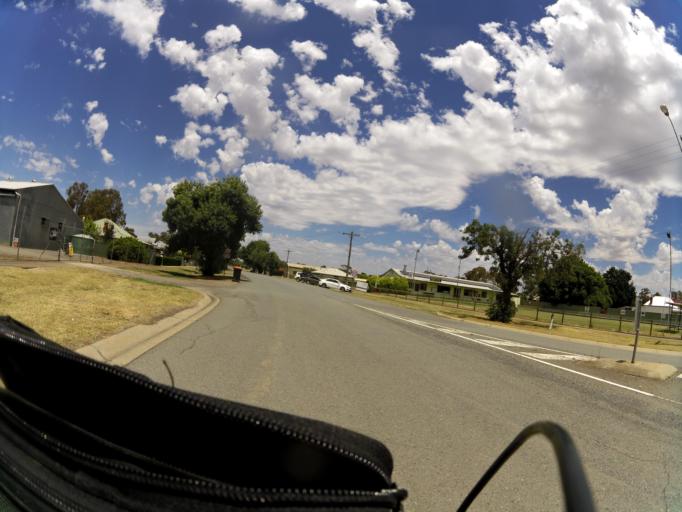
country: AU
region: Victoria
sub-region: Greater Shepparton
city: Shepparton
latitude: -36.6193
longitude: 145.2176
